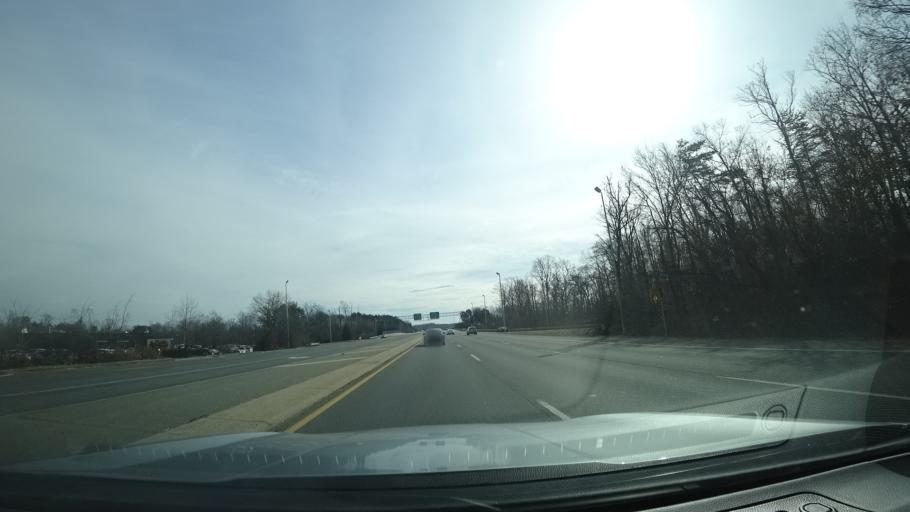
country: US
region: Virginia
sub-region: Prince William County
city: Dumfries
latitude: 38.5813
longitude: -77.3257
